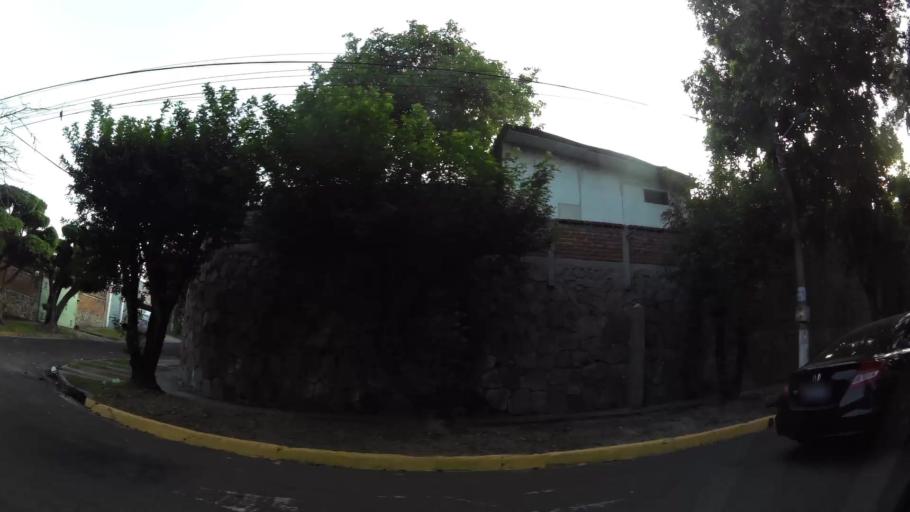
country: SV
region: La Libertad
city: Antiguo Cuscatlan
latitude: 13.7022
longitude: -89.2477
